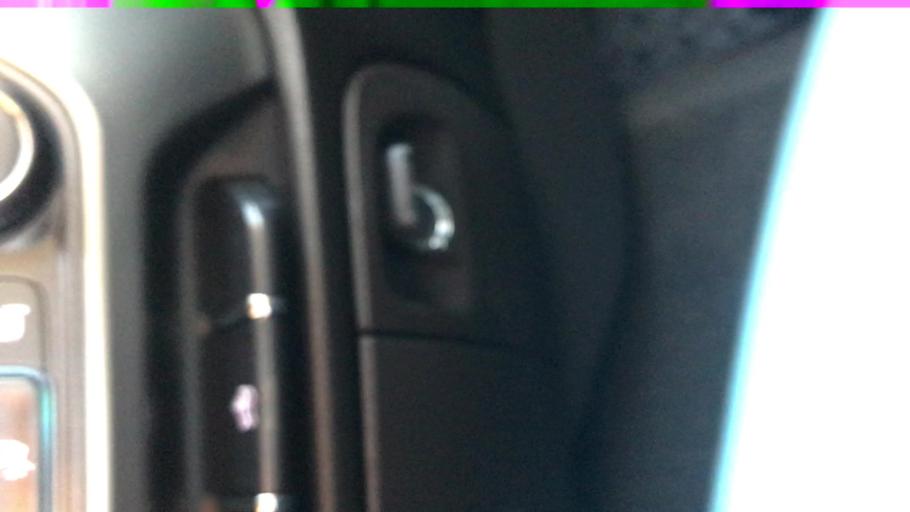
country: US
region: Texas
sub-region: Dallas County
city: Coppell
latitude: 32.9438
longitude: -97.0156
